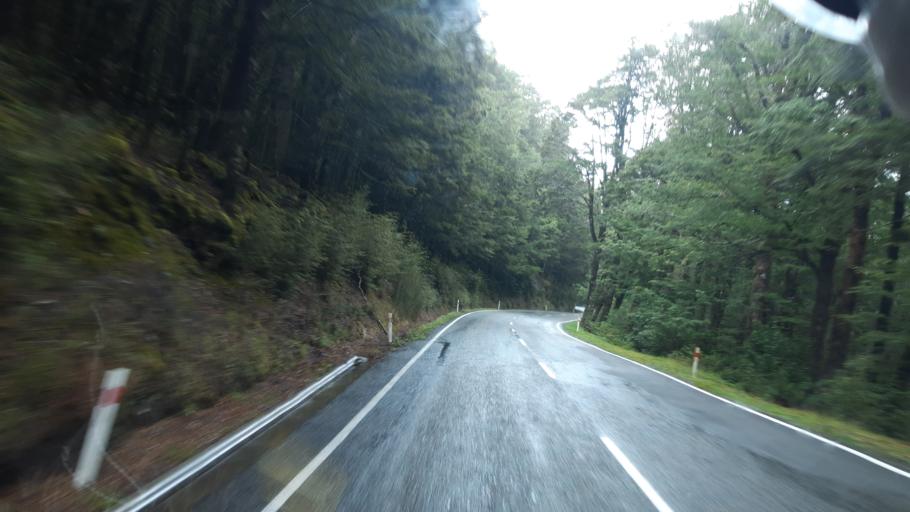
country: NZ
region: Canterbury
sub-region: Hurunui District
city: Amberley
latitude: -42.3763
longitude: 172.3589
